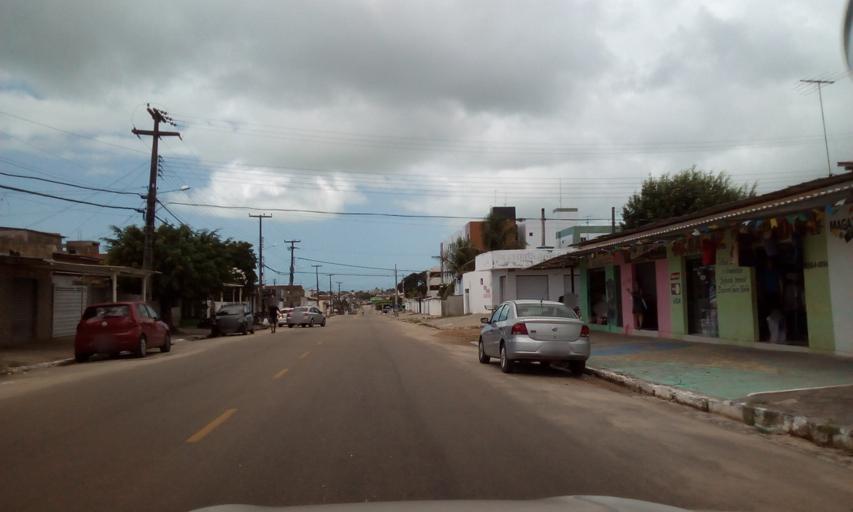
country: BR
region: Paraiba
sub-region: Conde
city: Conde
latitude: -7.2053
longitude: -34.8400
